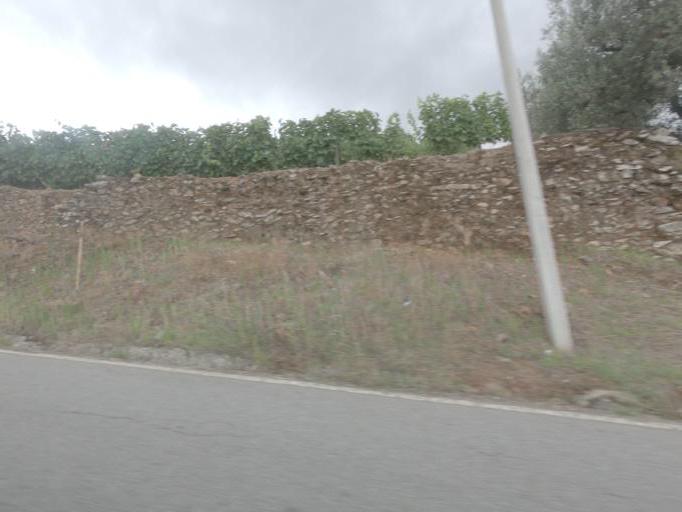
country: PT
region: Vila Real
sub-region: Sabrosa
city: Sabrosa
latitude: 41.2813
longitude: -7.5522
